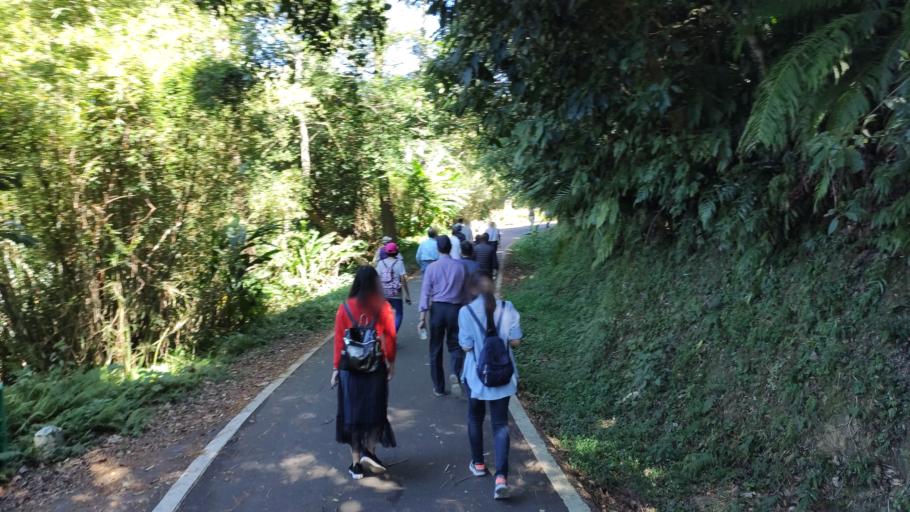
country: TW
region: Taiwan
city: Daxi
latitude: 24.8393
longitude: 121.3069
